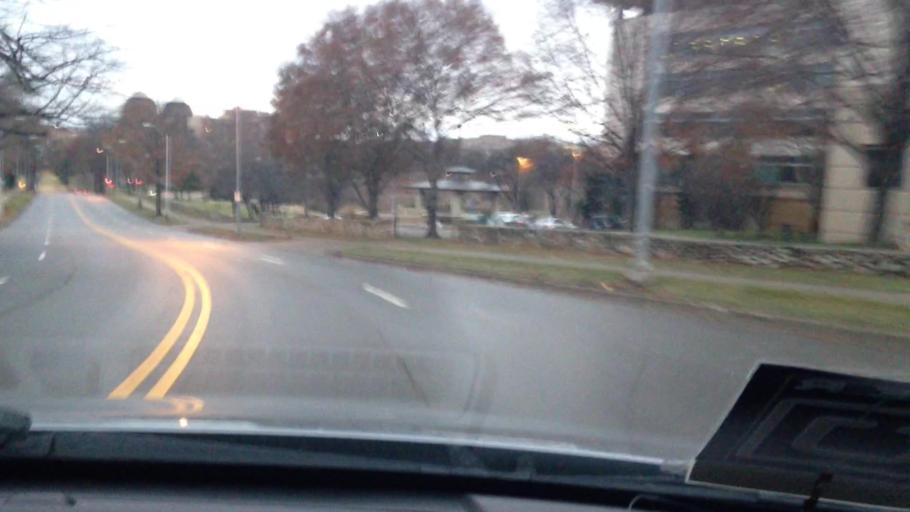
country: US
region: Kansas
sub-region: Johnson County
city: Westwood
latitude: 39.0364
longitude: -94.5758
